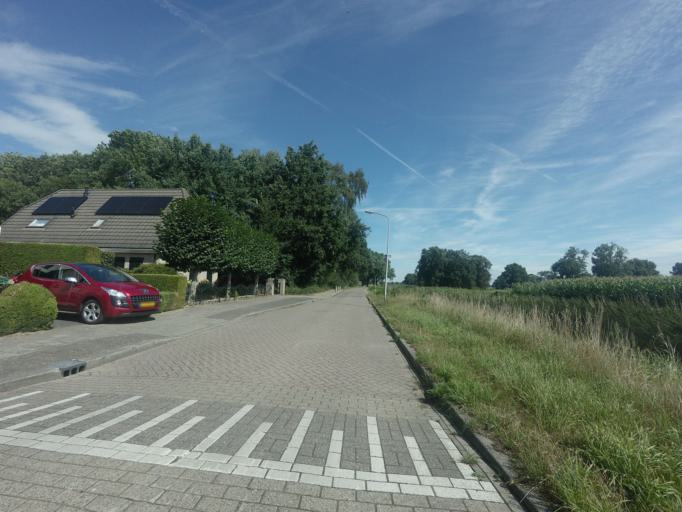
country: NL
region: Overijssel
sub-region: Gemeente Raalte
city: Raalte
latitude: 52.3990
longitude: 6.2939
